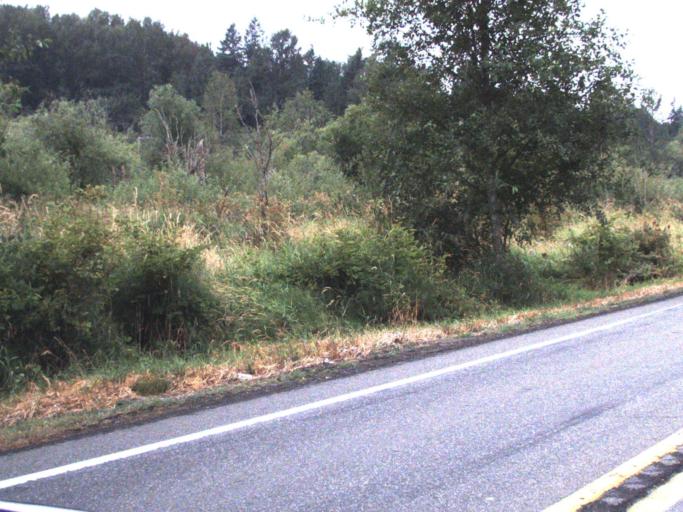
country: US
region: Washington
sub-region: King County
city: Sammamish
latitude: 47.6529
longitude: -122.0508
